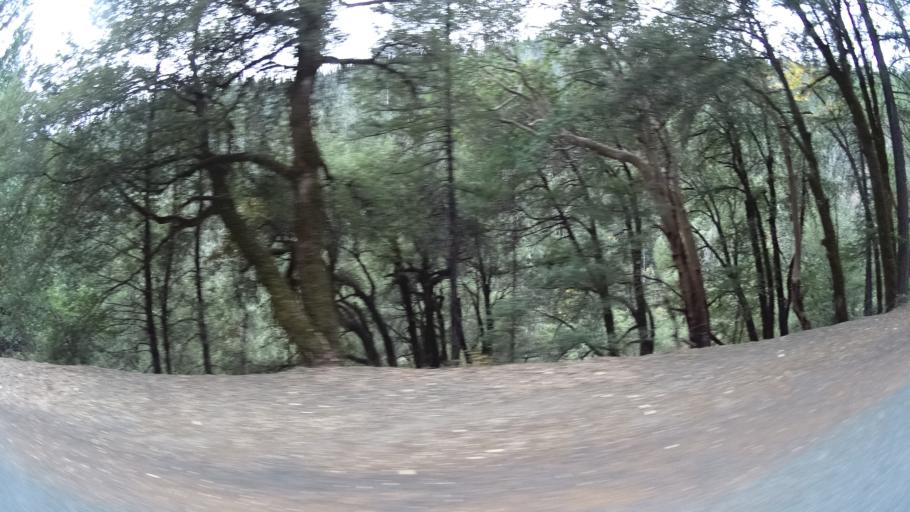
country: US
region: California
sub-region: Siskiyou County
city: Happy Camp
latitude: 41.7538
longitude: -123.3637
